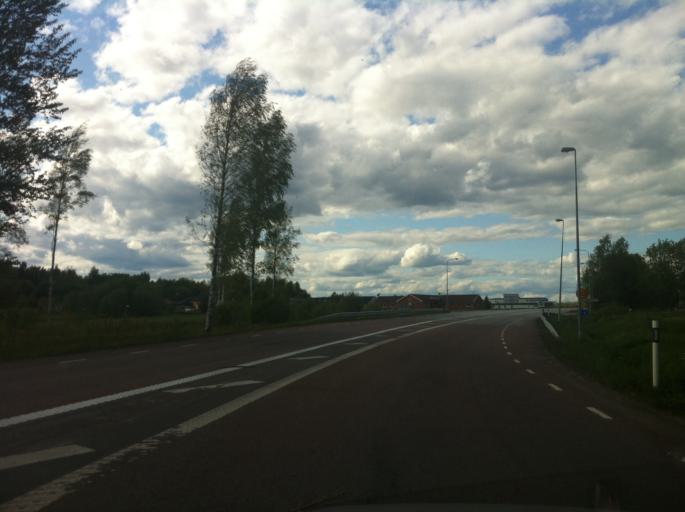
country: SE
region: Vaermland
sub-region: Storfors Kommun
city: Storfors
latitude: 59.5405
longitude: 14.2792
